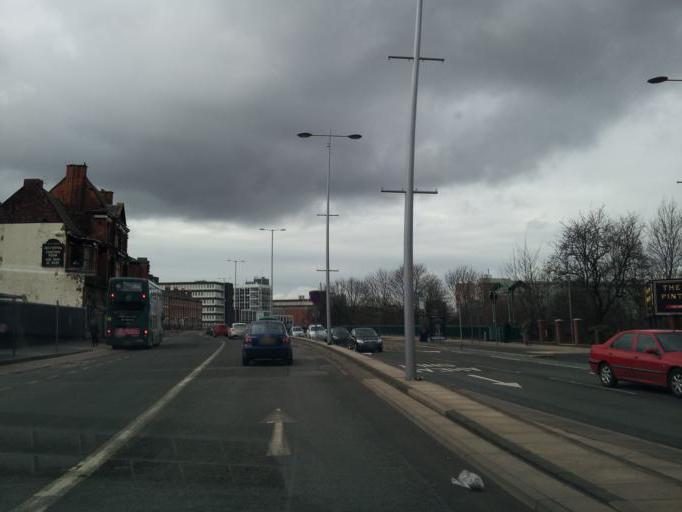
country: GB
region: England
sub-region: Manchester
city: Hulme
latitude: 53.4833
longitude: -2.2652
